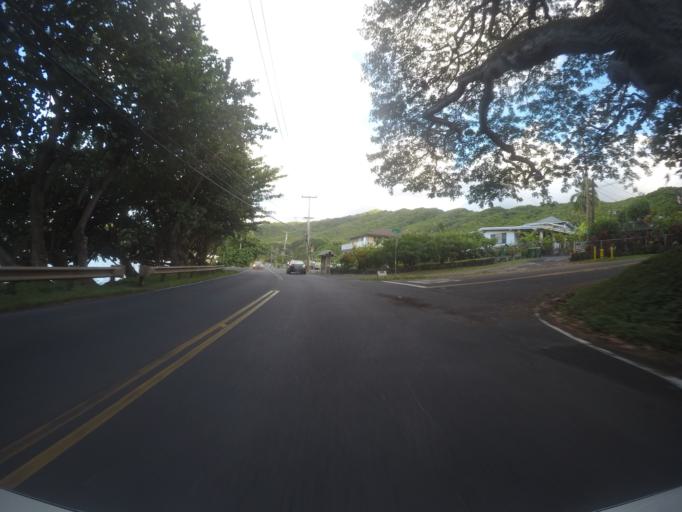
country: US
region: Hawaii
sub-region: Honolulu County
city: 'Ahuimanu
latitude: 21.4544
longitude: -157.8264
